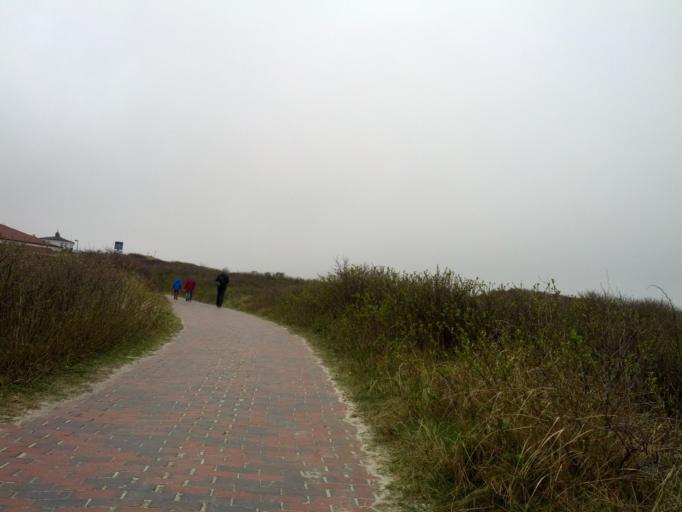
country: DE
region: Lower Saxony
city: Langeoog
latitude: 53.7525
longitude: 7.4805
